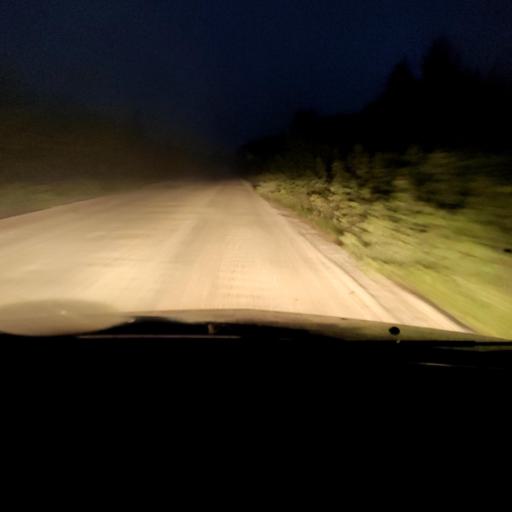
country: RU
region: Bashkortostan
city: Kabakovo
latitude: 54.6821
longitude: 56.2720
